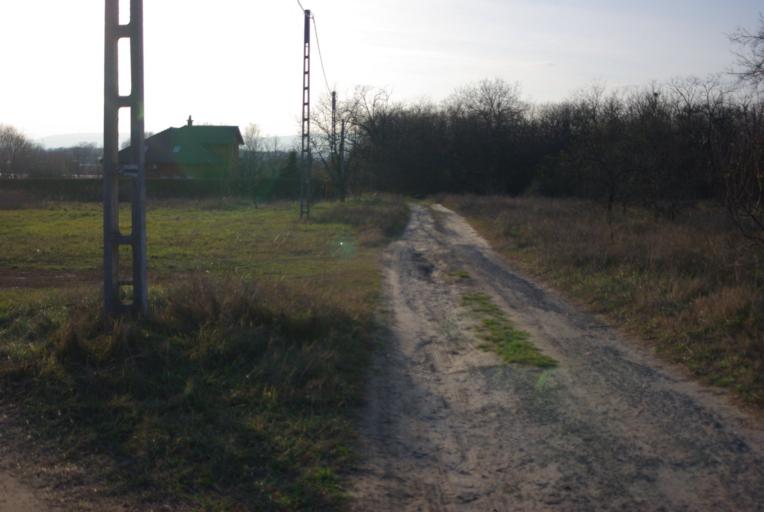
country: HU
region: Pest
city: Fot
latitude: 47.6155
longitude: 19.2105
